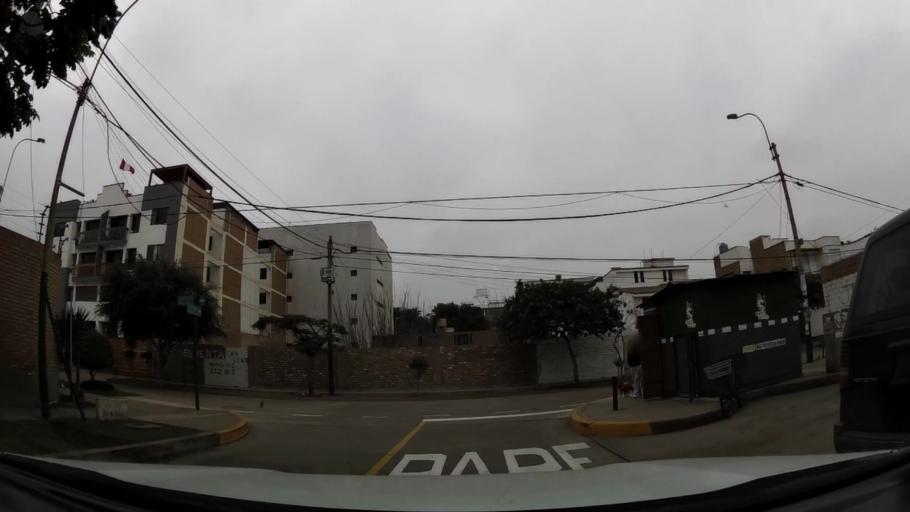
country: PE
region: Lima
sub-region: Lima
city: Surco
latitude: -12.1332
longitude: -77.0042
